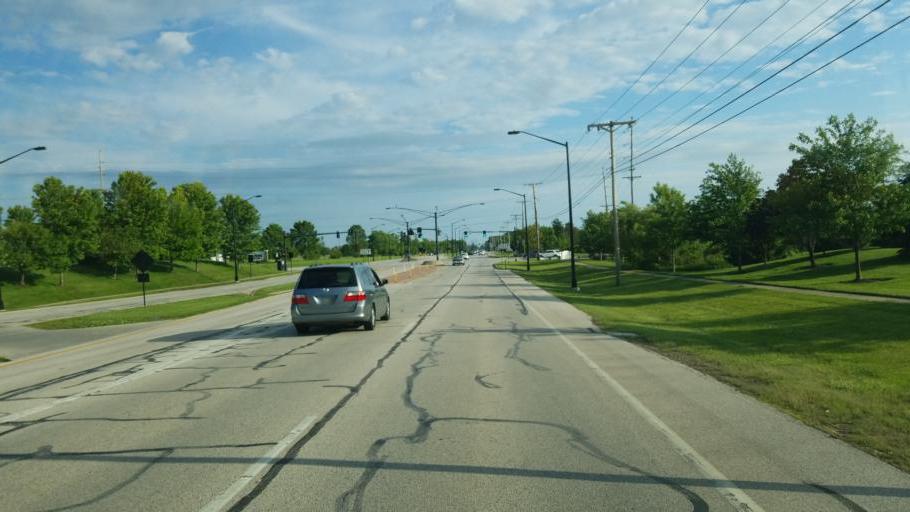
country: US
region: Ohio
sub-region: Summit County
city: Hudson
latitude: 41.2188
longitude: -81.4405
